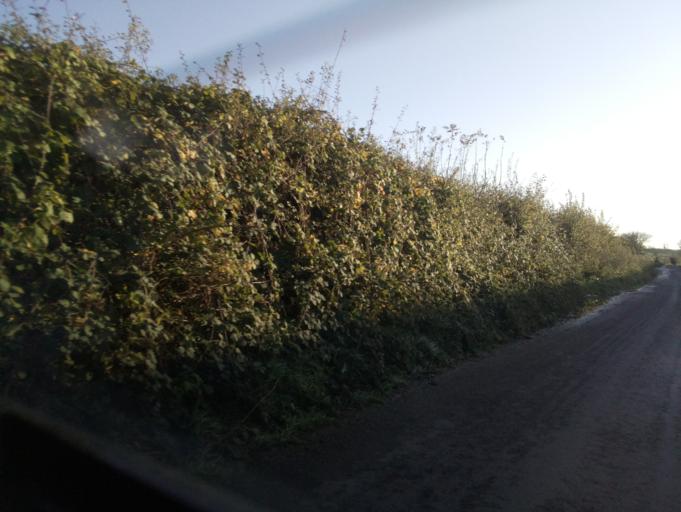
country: GB
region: England
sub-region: Somerset
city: Milborne Port
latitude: 50.9959
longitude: -2.4578
